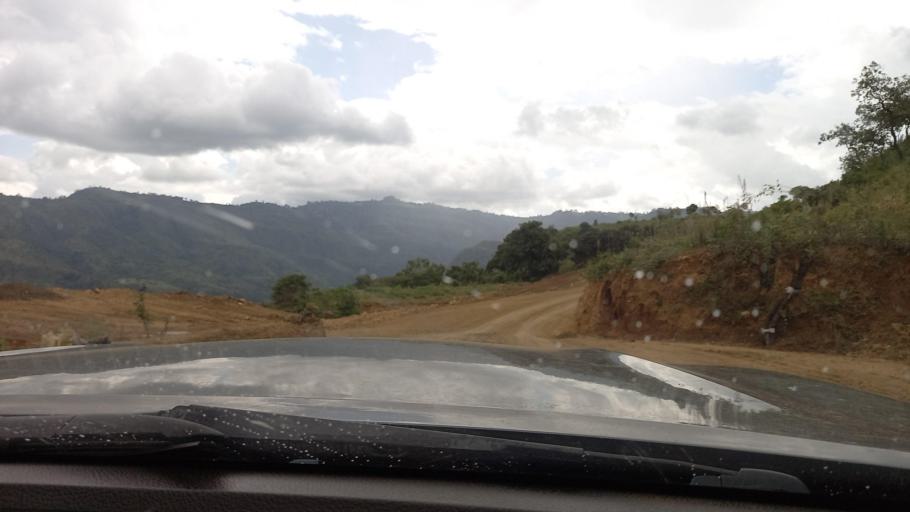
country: ET
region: Southern Nations, Nationalities, and People's Region
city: Mizan Teferi
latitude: 6.2034
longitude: 35.6560
